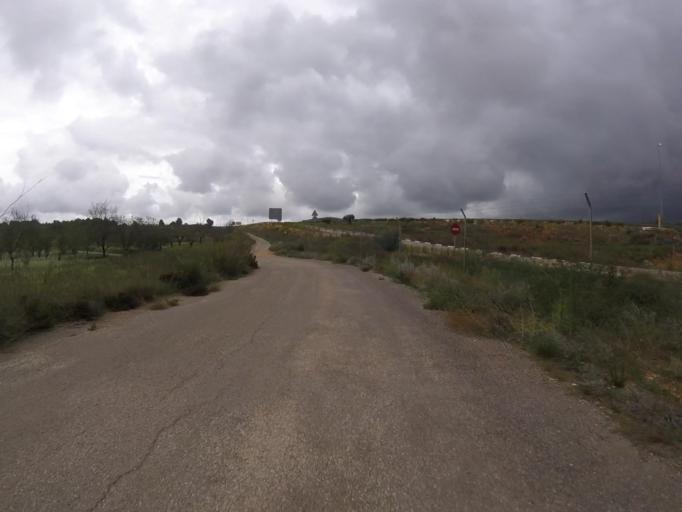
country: ES
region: Valencia
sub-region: Provincia de Castello
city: Benlloch
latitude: 40.1970
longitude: 0.0530
